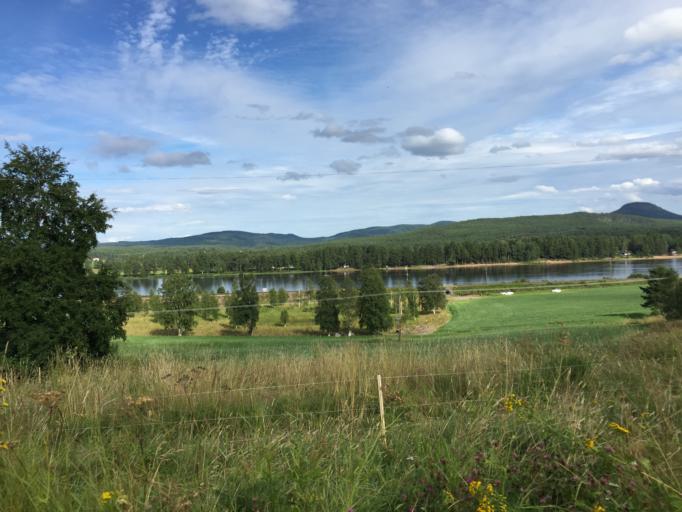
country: SE
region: Gaevleborg
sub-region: Ljusdals Kommun
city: Jaervsoe
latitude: 61.7449
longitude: 16.1610
